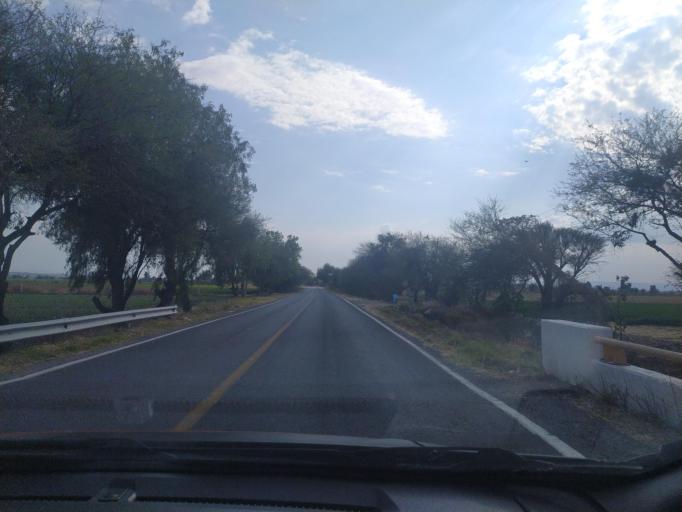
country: MX
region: Guanajuato
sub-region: San Francisco del Rincon
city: San Ignacio de Hidalgo
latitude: 20.9197
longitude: -101.8560
